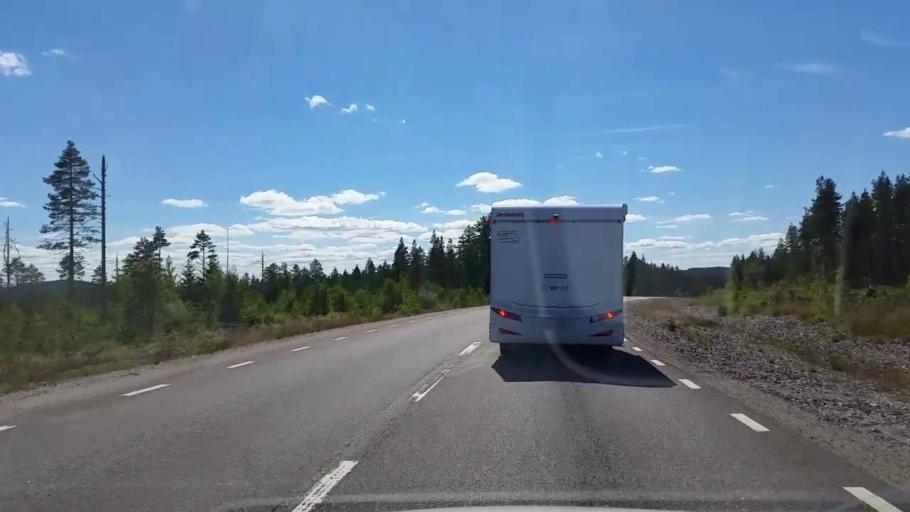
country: SE
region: Gaevleborg
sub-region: Bollnas Kommun
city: Vittsjo
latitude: 61.1018
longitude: 15.8546
